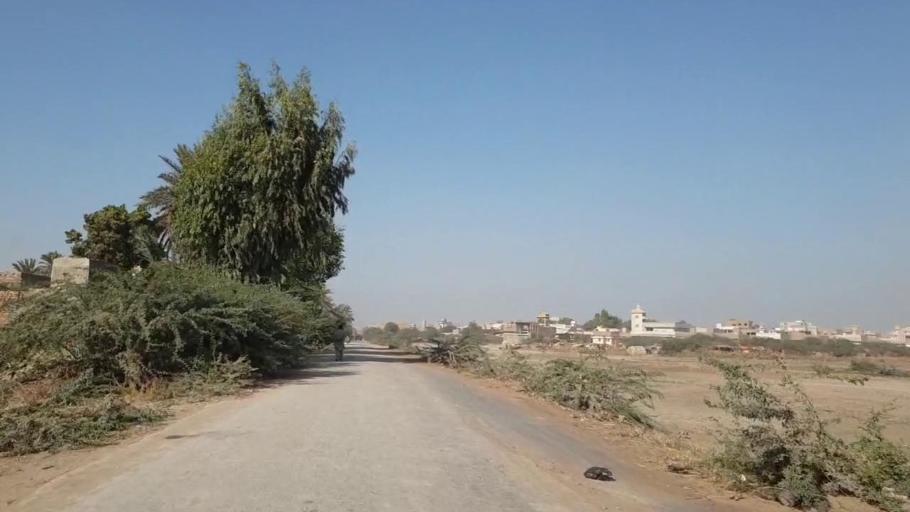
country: PK
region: Sindh
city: Digri
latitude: 25.1462
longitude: 69.1116
